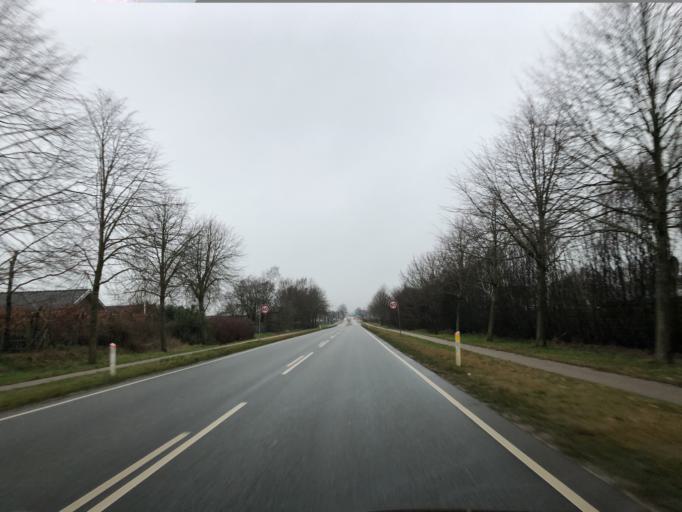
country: DK
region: Central Jutland
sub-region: Herning Kommune
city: Lind
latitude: 56.0996
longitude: 8.9800
